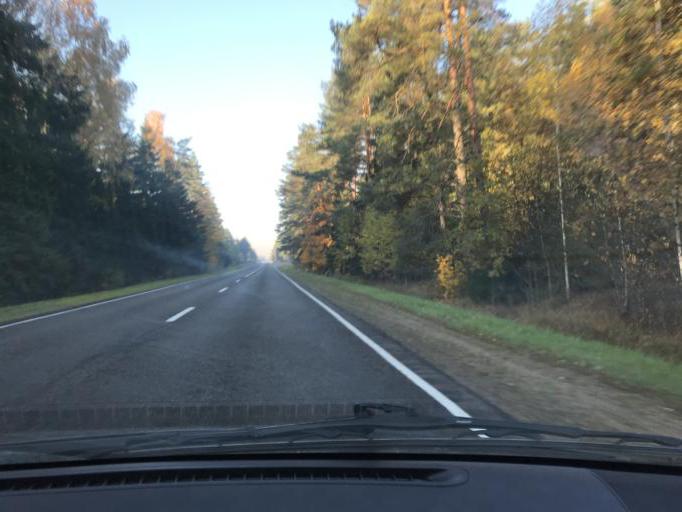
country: BY
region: Brest
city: Baranovichi
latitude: 52.9238
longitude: 25.9966
